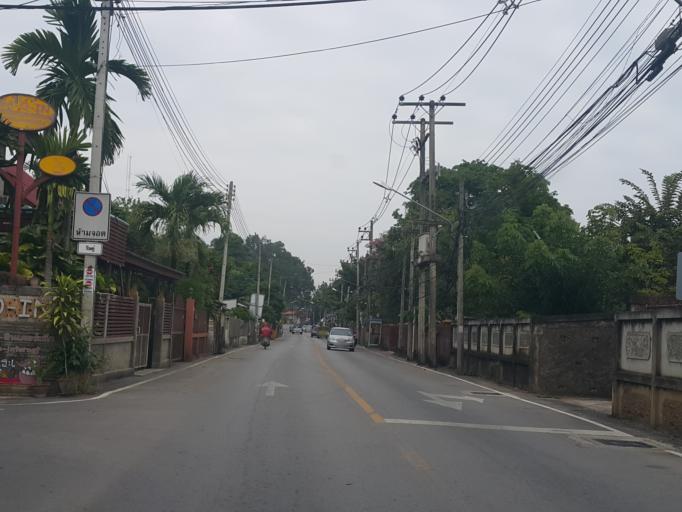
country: TH
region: Lampang
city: Lampang
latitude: 18.2942
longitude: 99.5092
